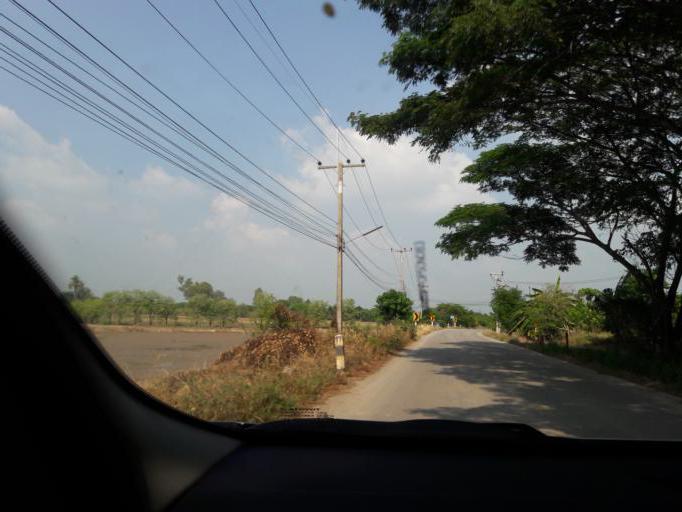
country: TH
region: Ang Thong
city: Ang Thong
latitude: 14.5466
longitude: 100.4254
